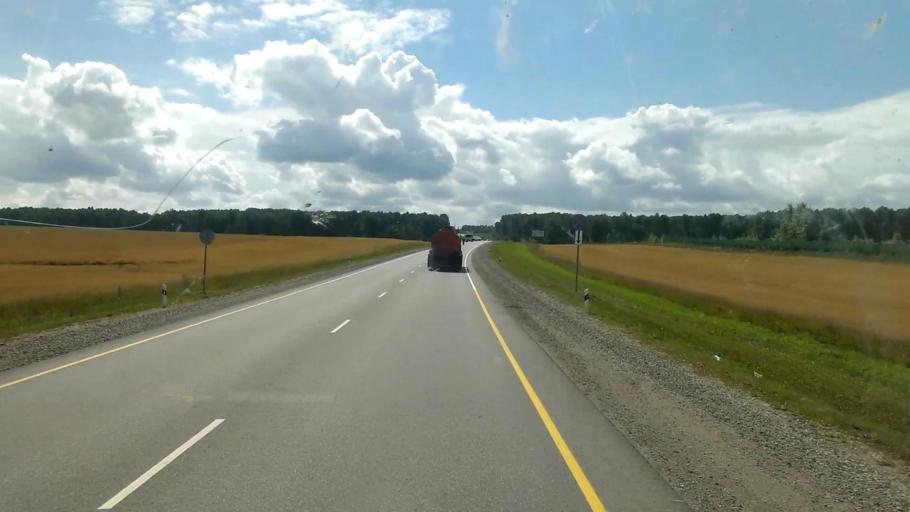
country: RU
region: Altai Krai
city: Troitskoye
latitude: 52.9883
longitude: 84.7432
